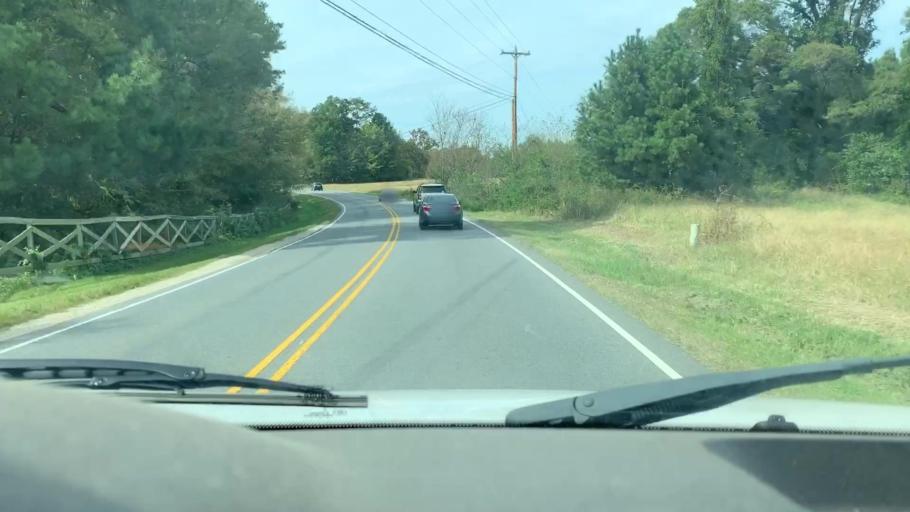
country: US
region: North Carolina
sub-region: Mecklenburg County
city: Huntersville
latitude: 35.4457
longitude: -80.7817
